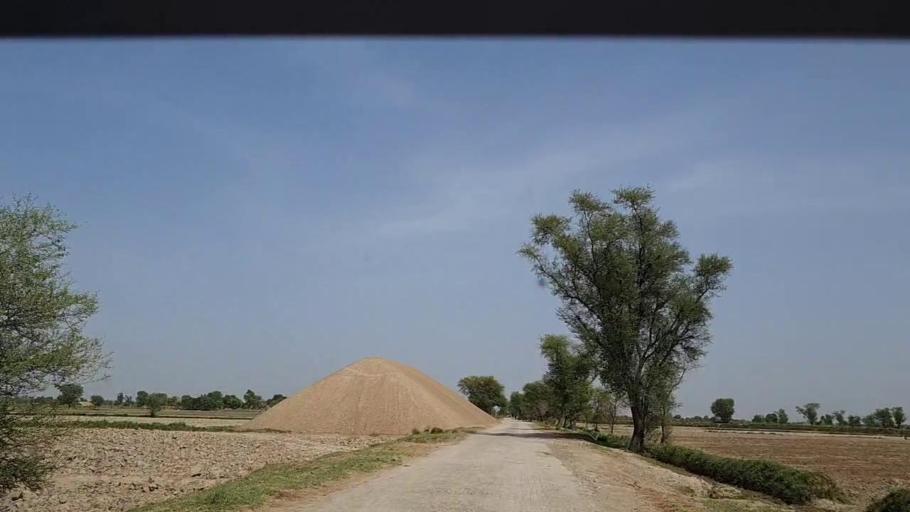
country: PK
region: Sindh
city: Phulji
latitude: 26.9563
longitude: 67.7085
